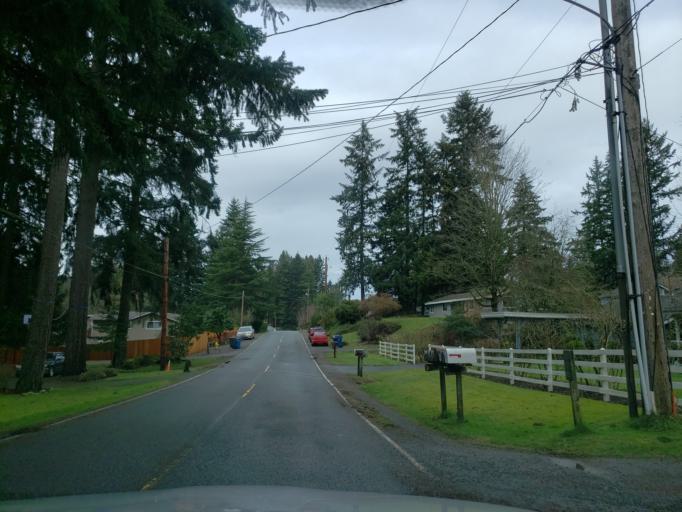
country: US
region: Washington
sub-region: Snohomish County
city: Lynnwood
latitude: 47.8155
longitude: -122.3426
